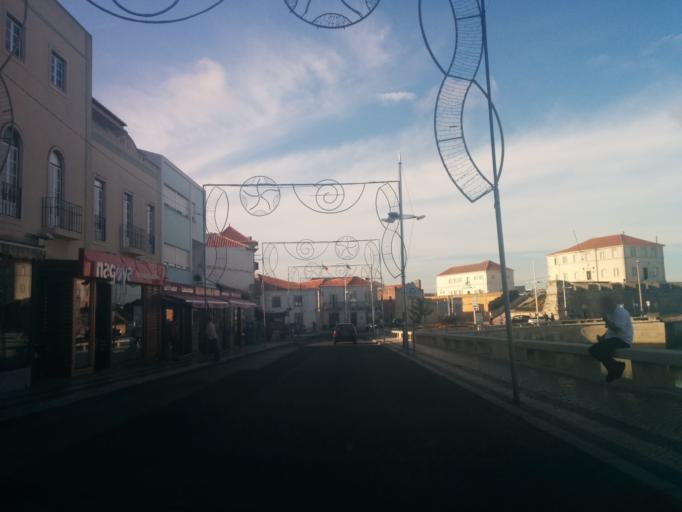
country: PT
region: Leiria
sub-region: Peniche
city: Peniche
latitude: 39.3559
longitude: -9.3785
